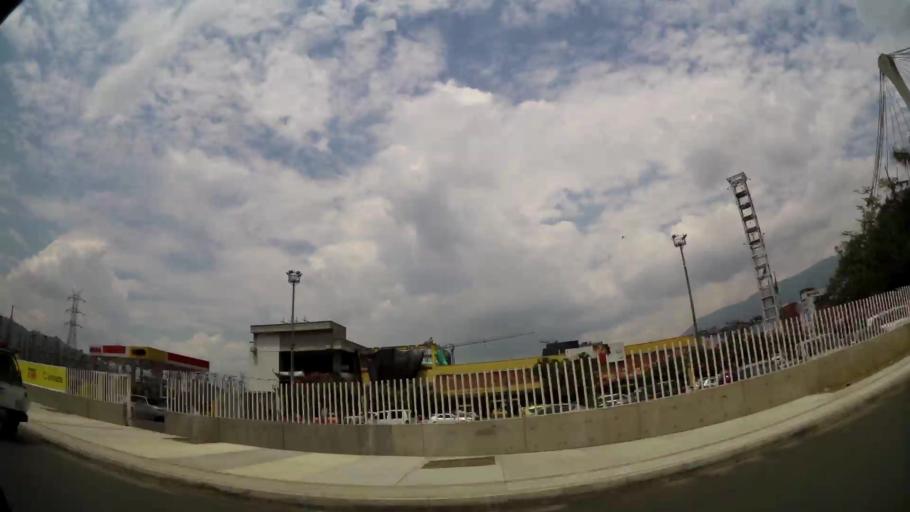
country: CO
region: Antioquia
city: Envigado
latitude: 6.1741
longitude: -75.5932
